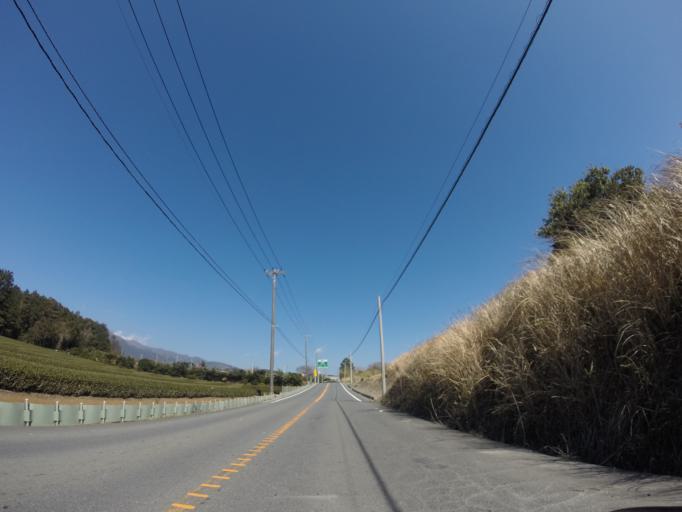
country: JP
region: Shizuoka
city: Numazu
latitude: 35.1405
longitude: 138.8371
